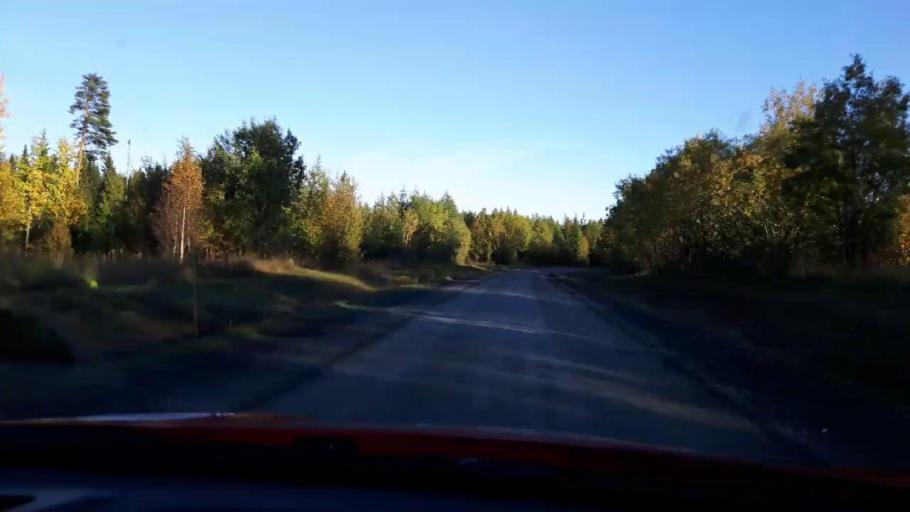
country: SE
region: Jaemtland
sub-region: OEstersunds Kommun
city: Lit
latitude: 63.6661
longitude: 14.7105
